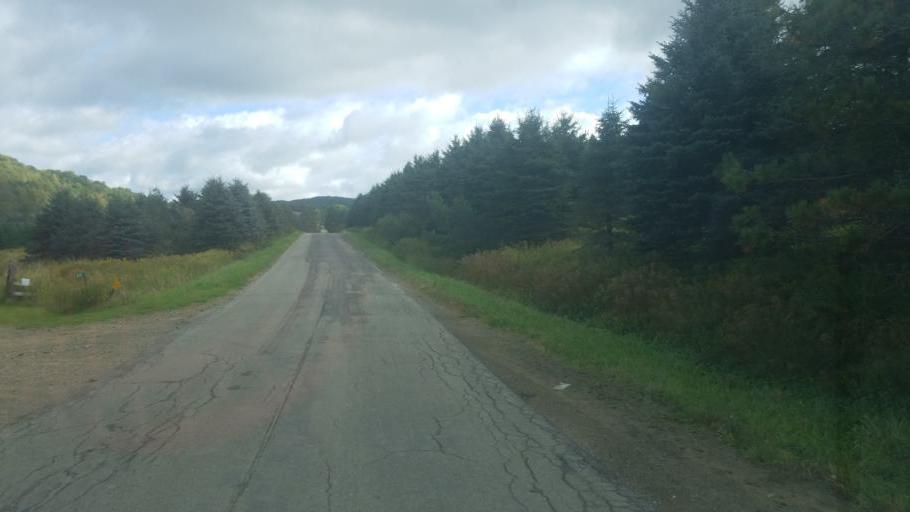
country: US
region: New York
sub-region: Cattaraugus County
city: Weston Mills
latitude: 42.1204
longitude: -78.3087
